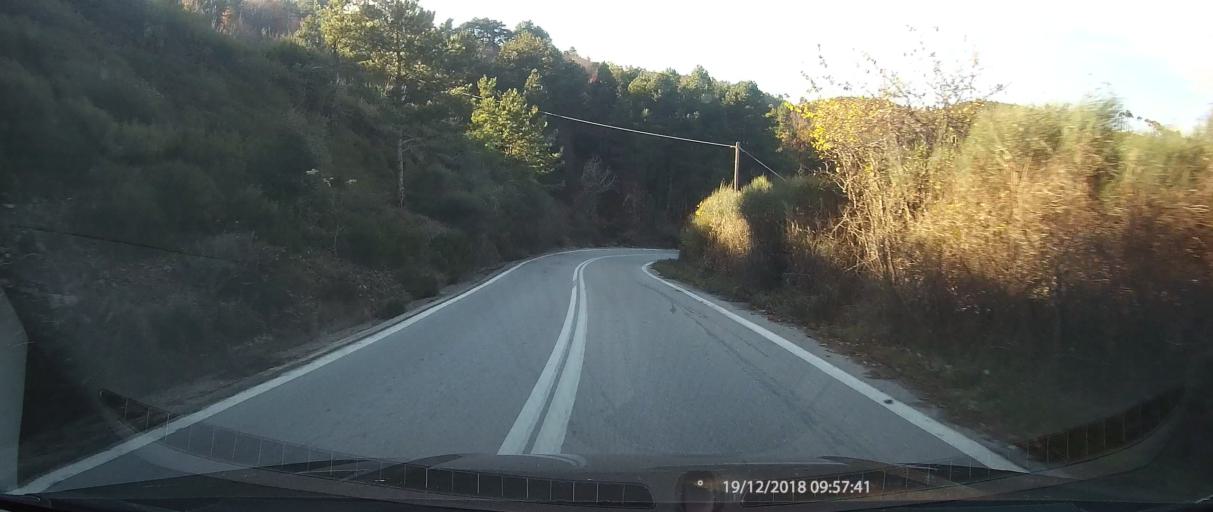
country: GR
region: Peloponnese
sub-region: Nomos Messinias
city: Paralia Vergas
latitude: 37.0885
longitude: 22.2367
